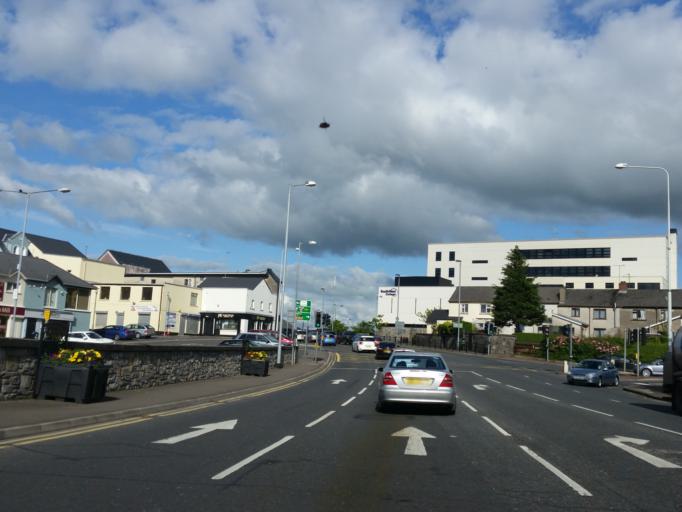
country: GB
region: Northern Ireland
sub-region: Fermanagh District
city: Enniskillen
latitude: 54.3435
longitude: -7.6336
